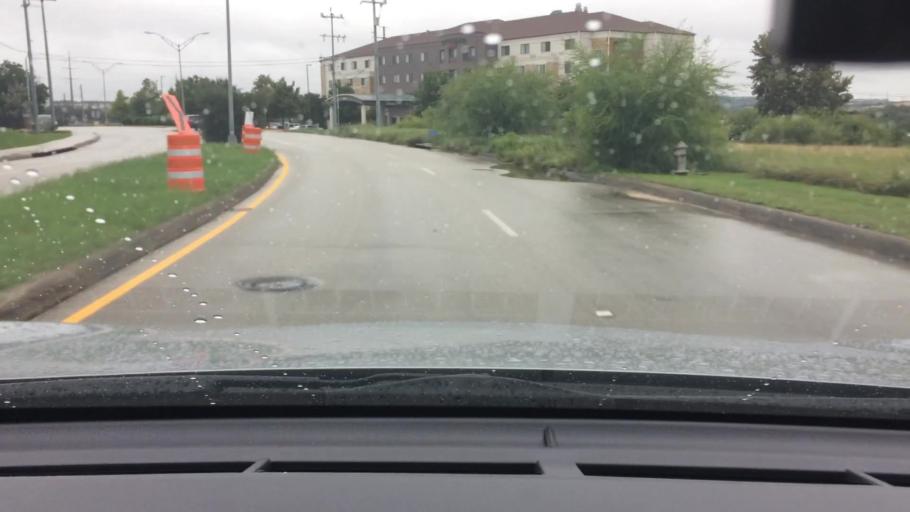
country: US
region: Texas
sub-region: Bexar County
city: Hollywood Park
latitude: 29.6131
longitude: -98.4632
